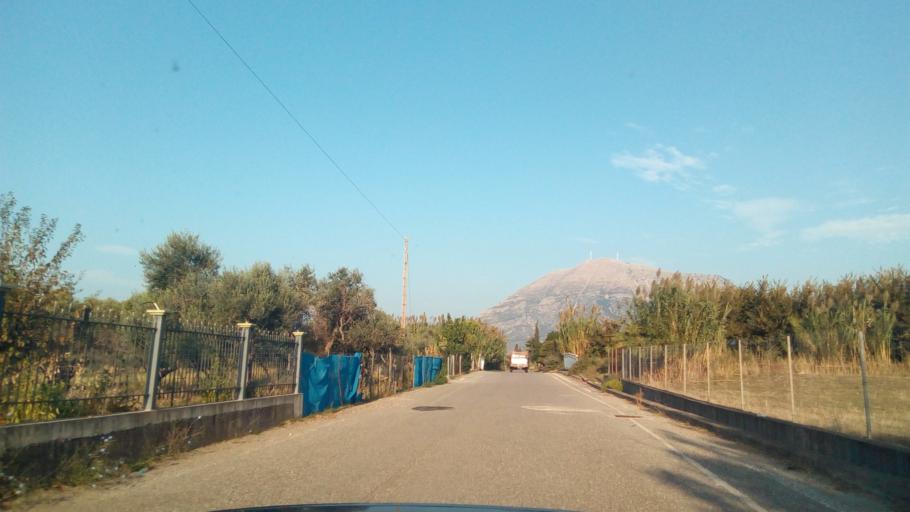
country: GR
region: West Greece
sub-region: Nomos Aitolias kai Akarnanias
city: Antirrio
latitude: 38.3344
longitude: 21.7548
